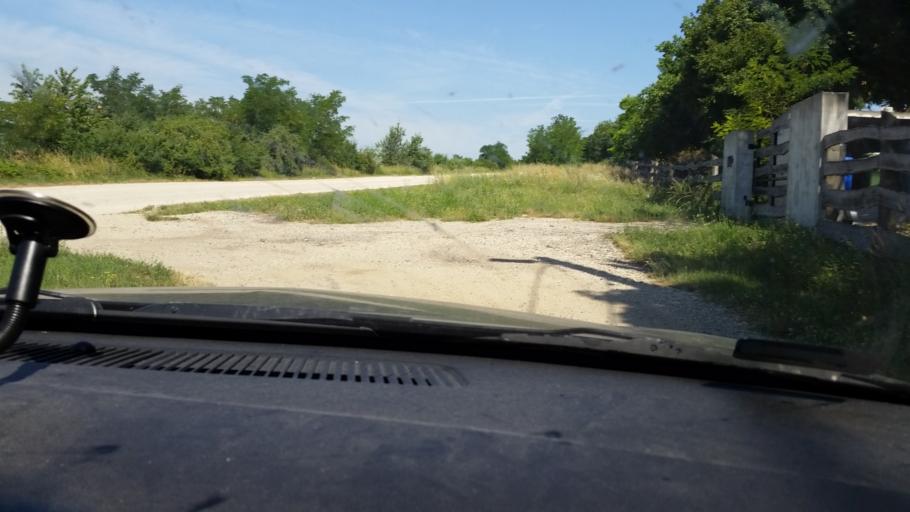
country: HU
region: Fejer
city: Many
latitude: 47.5314
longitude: 18.6037
